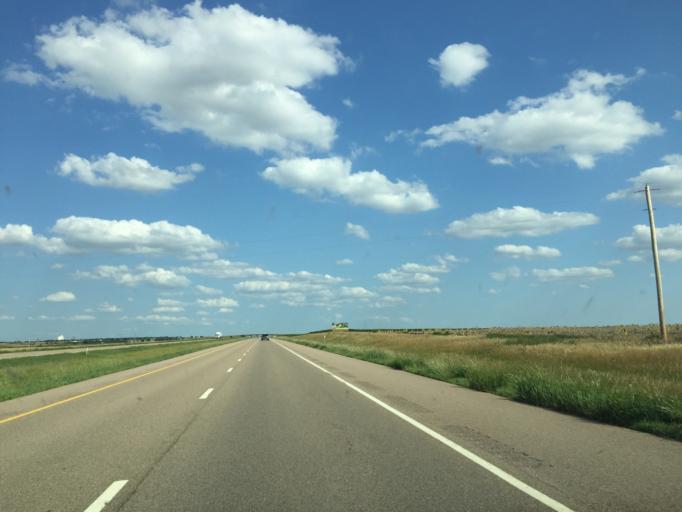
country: US
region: Kansas
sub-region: Gove County
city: Gove
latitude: 39.0824
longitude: -100.2940
